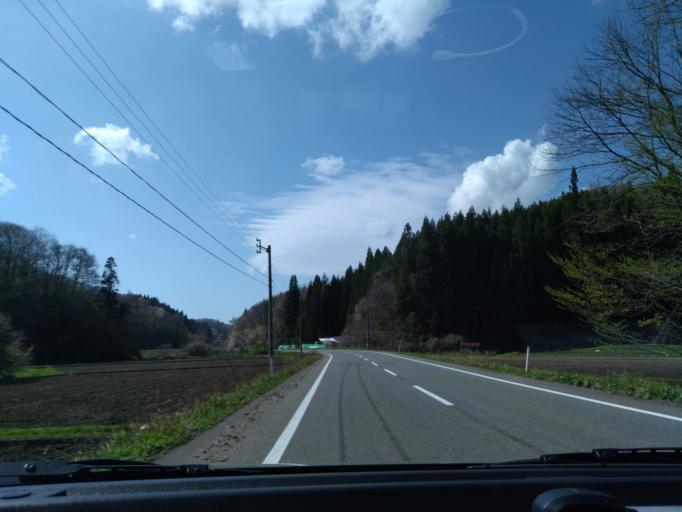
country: JP
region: Akita
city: Akita
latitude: 39.7040
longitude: 140.2142
